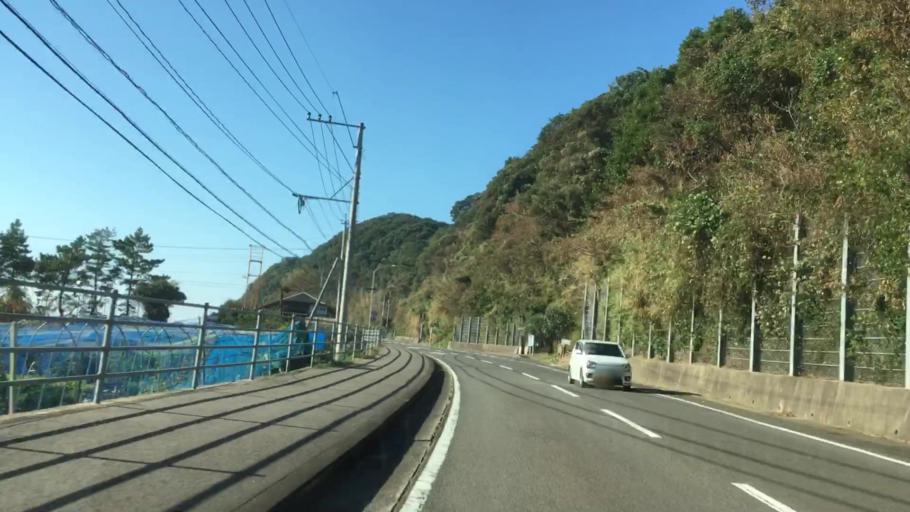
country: JP
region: Nagasaki
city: Sasebo
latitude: 33.0297
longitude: 129.6027
